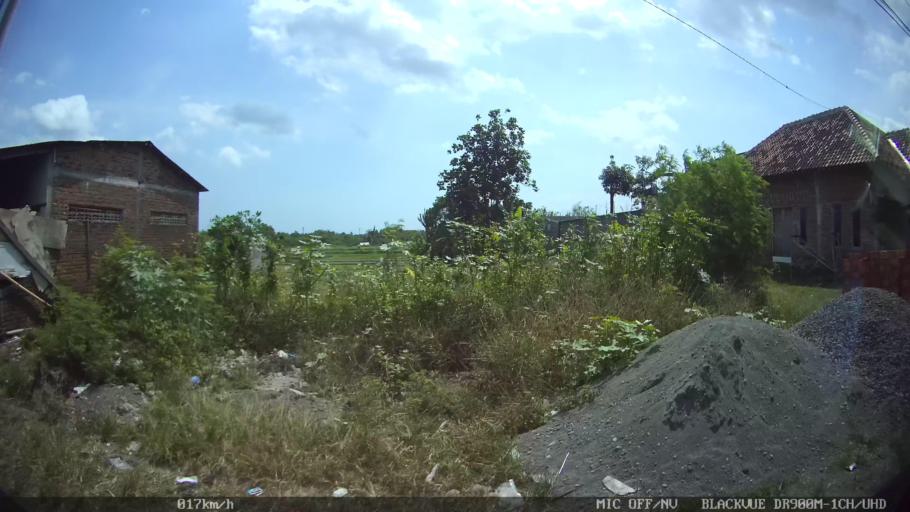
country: ID
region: Daerah Istimewa Yogyakarta
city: Kasihan
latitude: -7.8226
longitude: 110.3391
